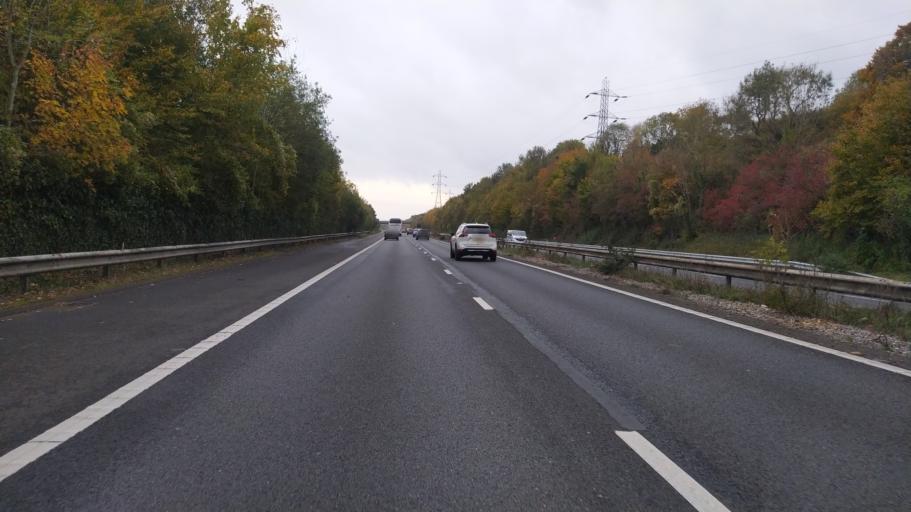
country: GB
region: England
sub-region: Hampshire
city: Cowplain
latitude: 50.9180
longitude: -0.9985
